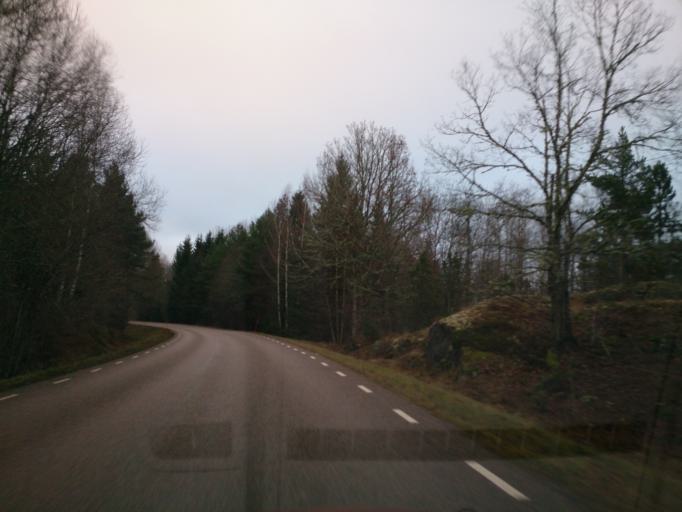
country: SE
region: OEstergoetland
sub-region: Atvidabergs Kommun
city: Atvidaberg
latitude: 58.2344
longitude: 16.0087
